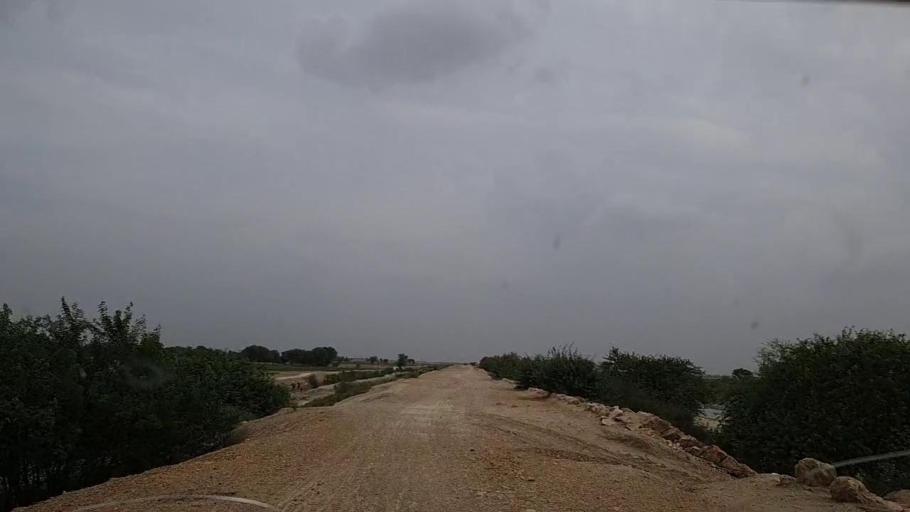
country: PK
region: Sindh
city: Johi
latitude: 26.7184
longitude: 67.5806
